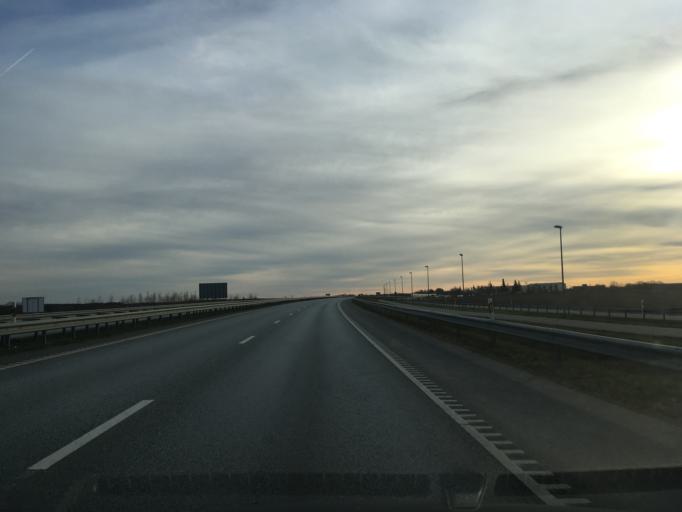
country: EE
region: Ida-Virumaa
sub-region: Johvi vald
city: Johvi
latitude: 59.3834
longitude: 27.3604
